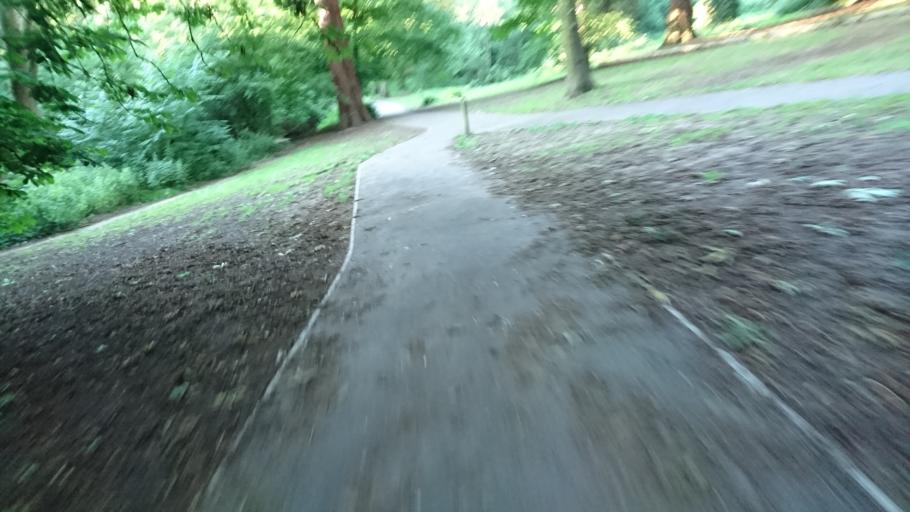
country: GB
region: England
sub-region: Greater London
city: Hendon
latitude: 51.6070
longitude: -0.1999
